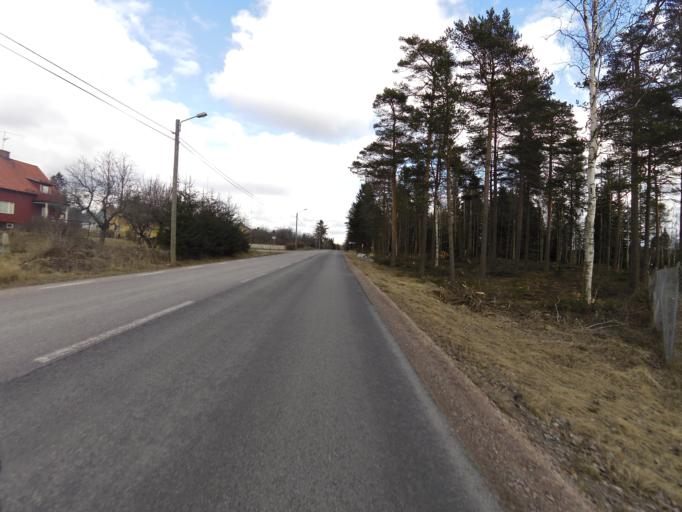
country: SE
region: Dalarna
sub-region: Avesta Kommun
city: Avesta
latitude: 60.3139
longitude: 16.1898
